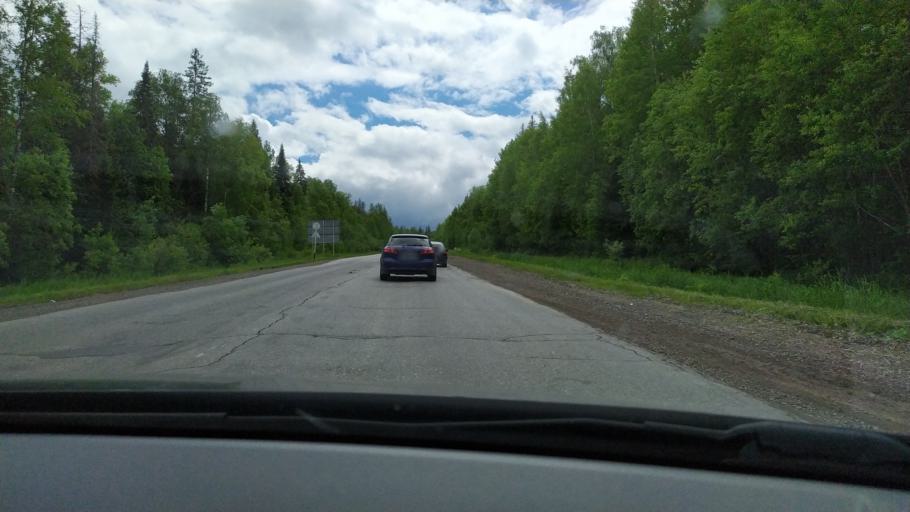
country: RU
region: Perm
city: Gremyachinsk
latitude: 58.4379
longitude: 57.8840
